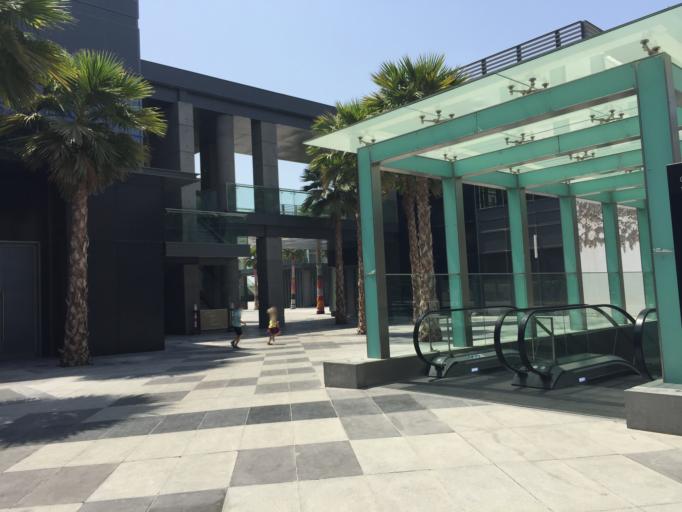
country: AE
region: Dubai
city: Dubai
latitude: 25.2070
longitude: 55.2618
